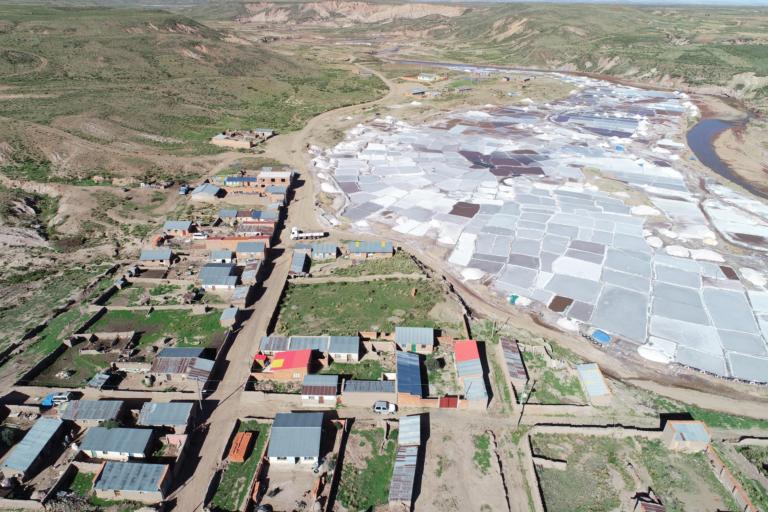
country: BO
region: La Paz
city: Patacamaya
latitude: -17.3005
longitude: -68.4819
